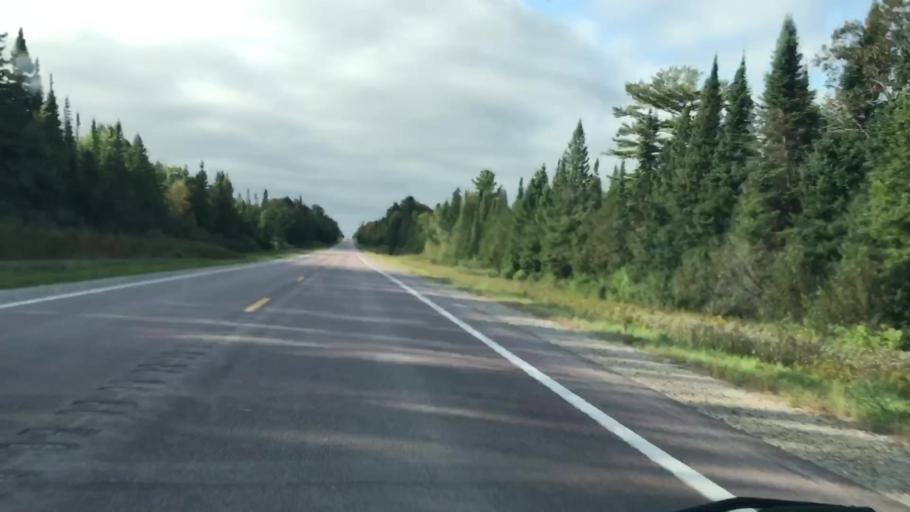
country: US
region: Michigan
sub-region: Luce County
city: Newberry
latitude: 46.2976
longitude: -85.5688
